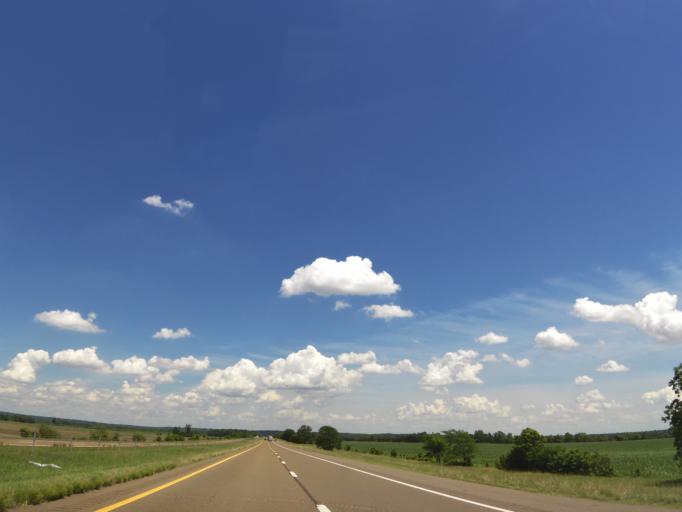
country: US
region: Missouri
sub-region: Pemiscot County
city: Caruthersville
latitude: 36.0885
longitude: -89.5648
